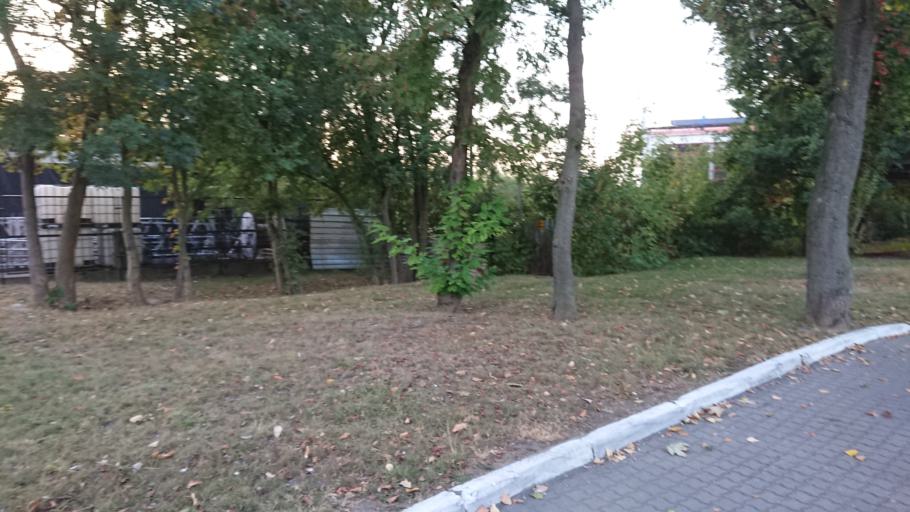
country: PL
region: Kujawsko-Pomorskie
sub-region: Powiat inowroclawski
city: Inowroclaw
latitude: 52.7901
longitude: 18.2484
